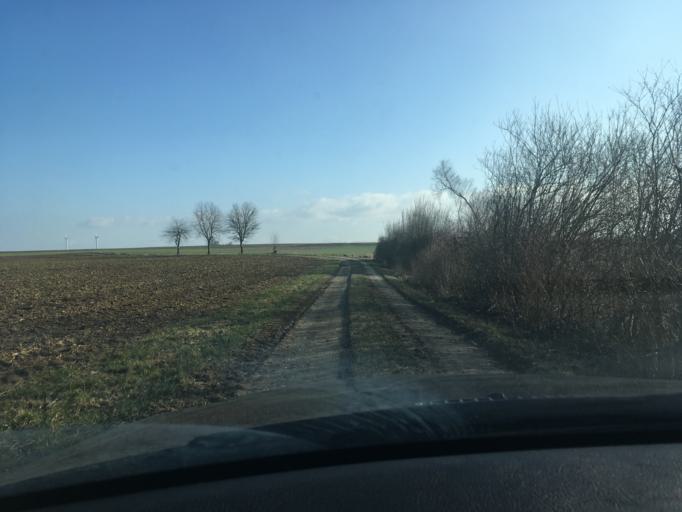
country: DE
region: Lower Saxony
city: Einbeck
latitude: 51.8007
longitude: 9.7892
